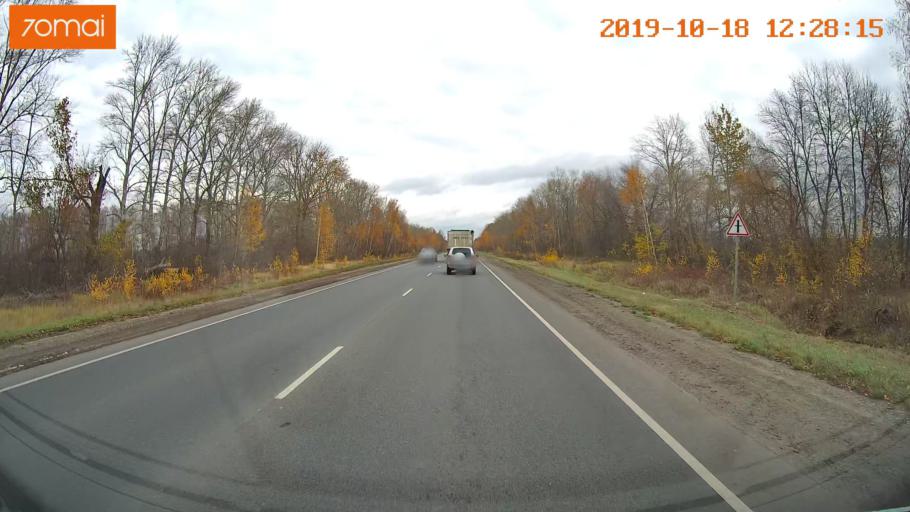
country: RU
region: Rjazan
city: Ryazan'
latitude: 54.5707
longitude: 39.5655
